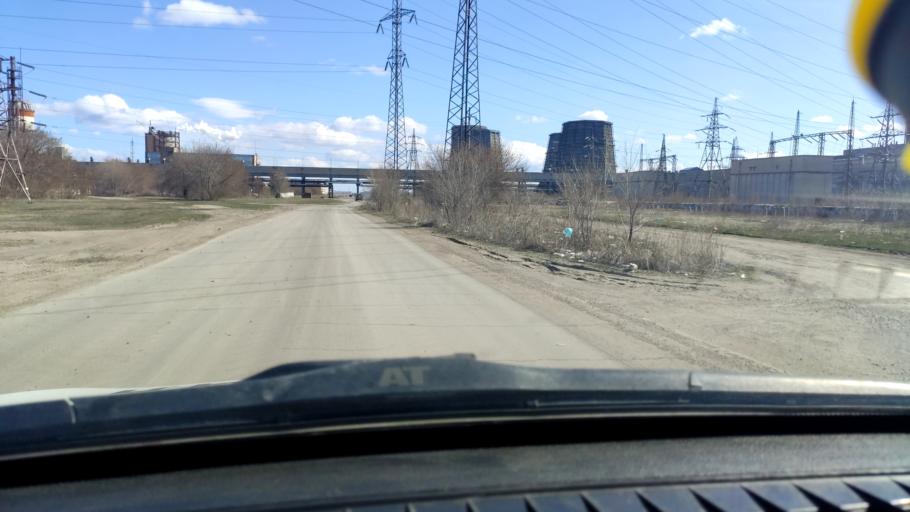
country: RU
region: Samara
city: Tol'yatti
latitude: 53.5506
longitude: 49.4524
